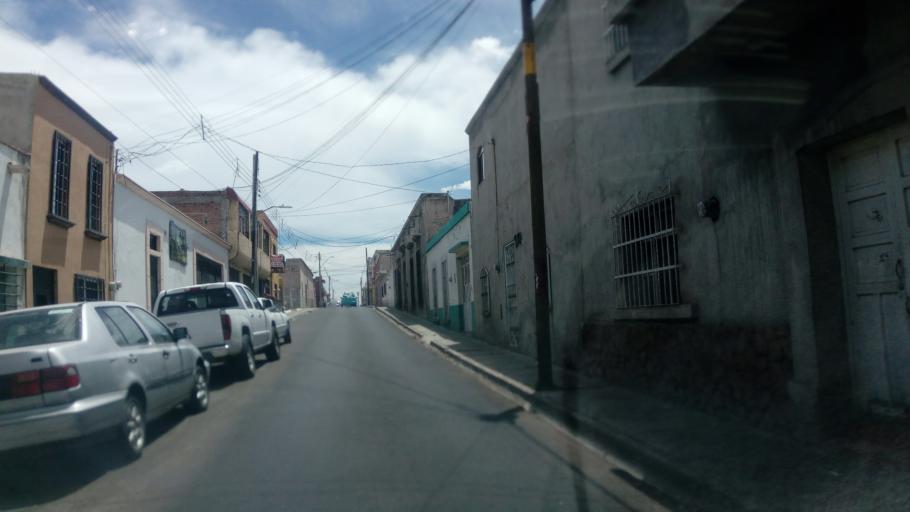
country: MX
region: Durango
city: Victoria de Durango
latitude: 24.0157
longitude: -104.6699
